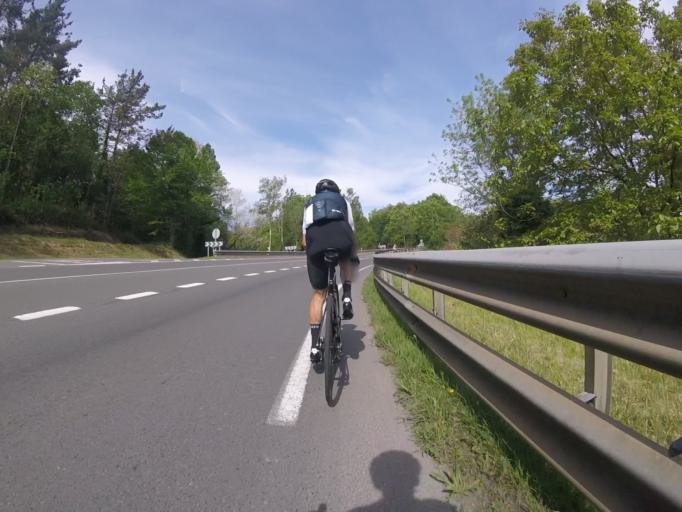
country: ES
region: Basque Country
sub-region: Provincia de Guipuzcoa
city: Cestona
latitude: 43.2547
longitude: -2.2667
